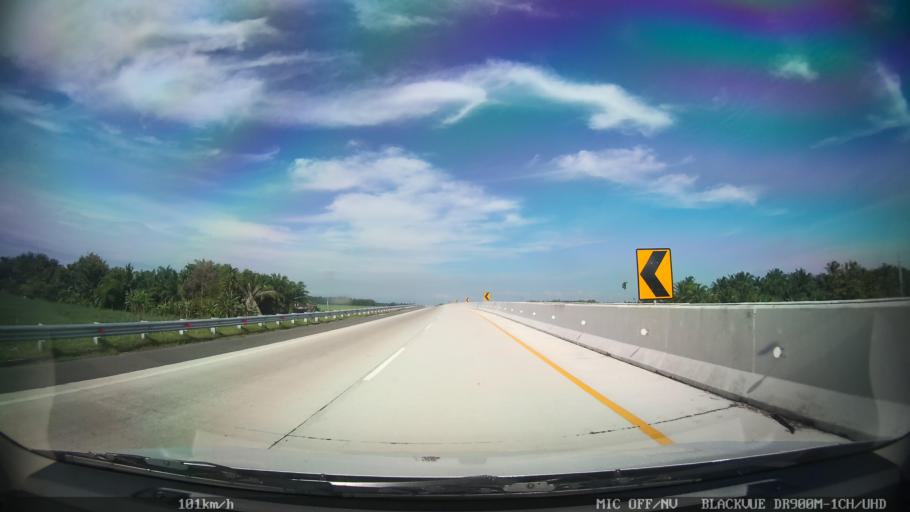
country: ID
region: North Sumatra
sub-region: Kabupaten Langkat
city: Stabat
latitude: 3.7135
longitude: 98.5257
